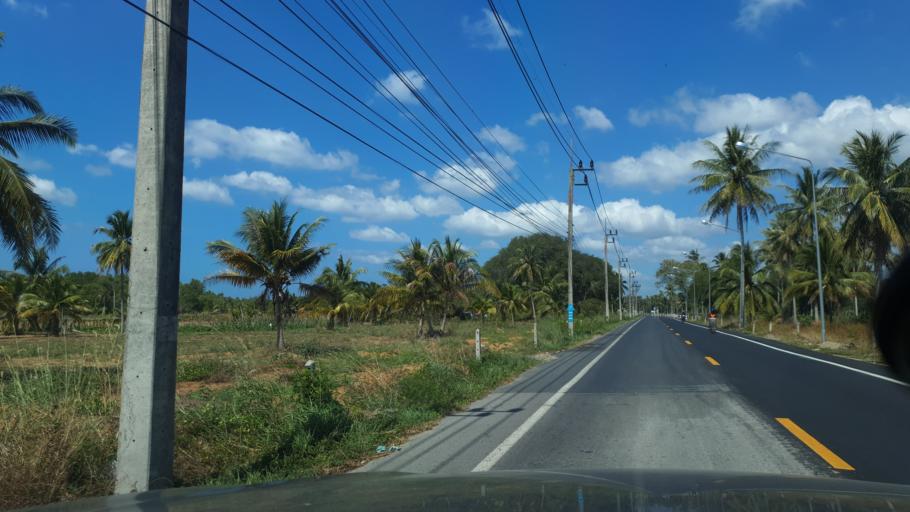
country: TH
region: Phuket
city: Thalang
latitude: 8.1463
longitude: 98.3060
